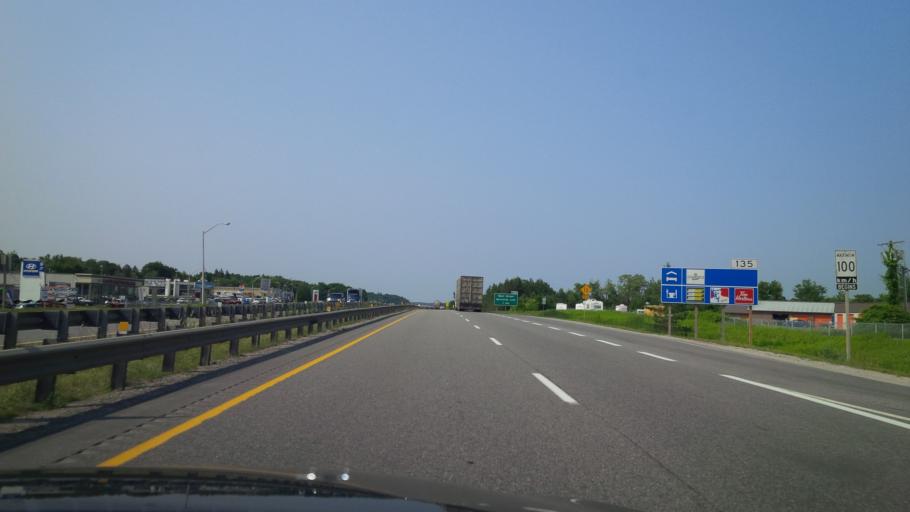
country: CA
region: Ontario
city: Orillia
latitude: 44.6395
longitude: -79.4253
